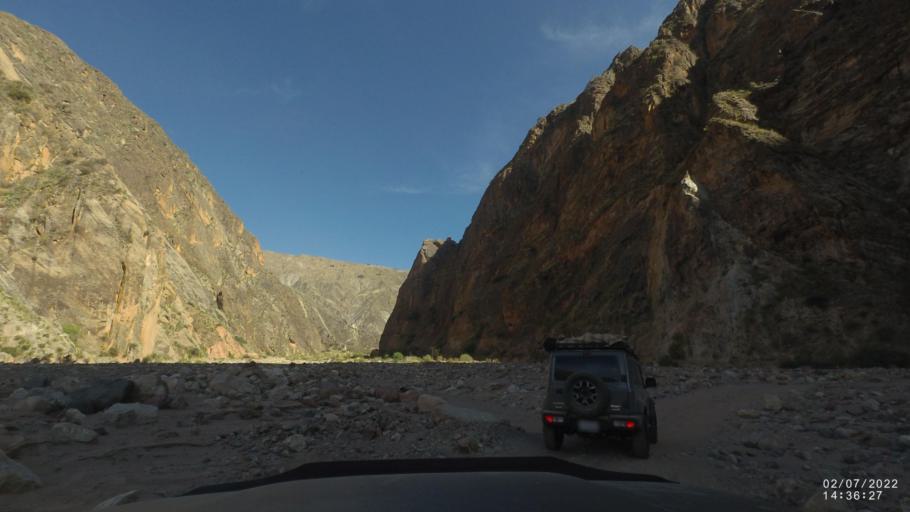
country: BO
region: Cochabamba
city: Irpa Irpa
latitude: -17.8406
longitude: -66.4181
